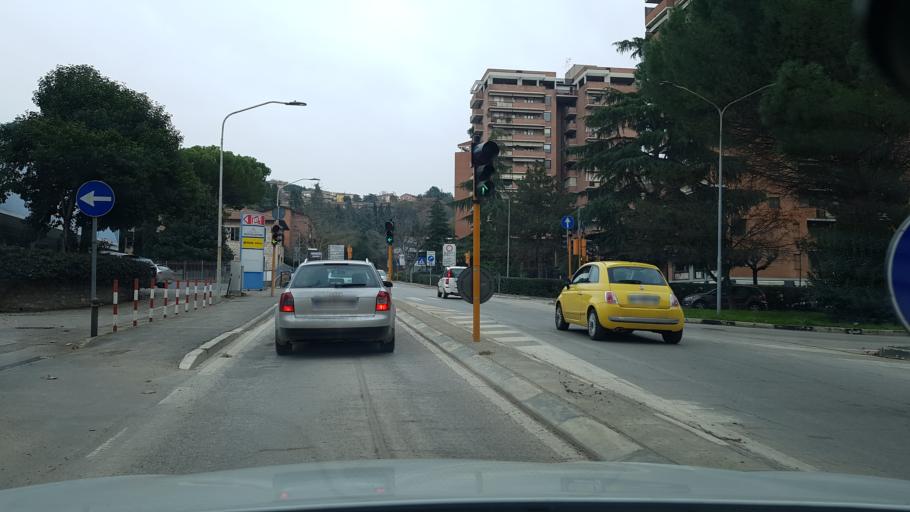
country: IT
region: Umbria
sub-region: Provincia di Perugia
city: Perugia
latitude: 43.1071
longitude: 12.3664
